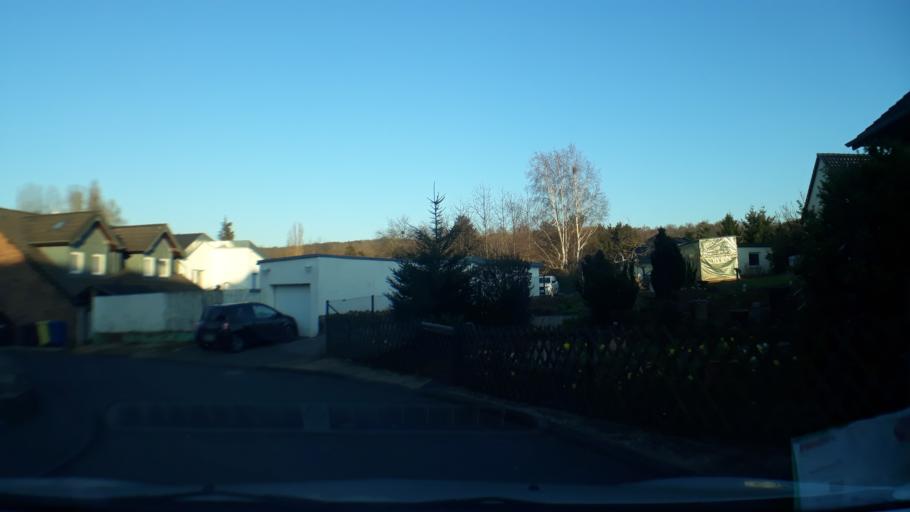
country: DE
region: North Rhine-Westphalia
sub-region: Regierungsbezirk Koln
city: Kall
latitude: 50.5672
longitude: 6.5980
